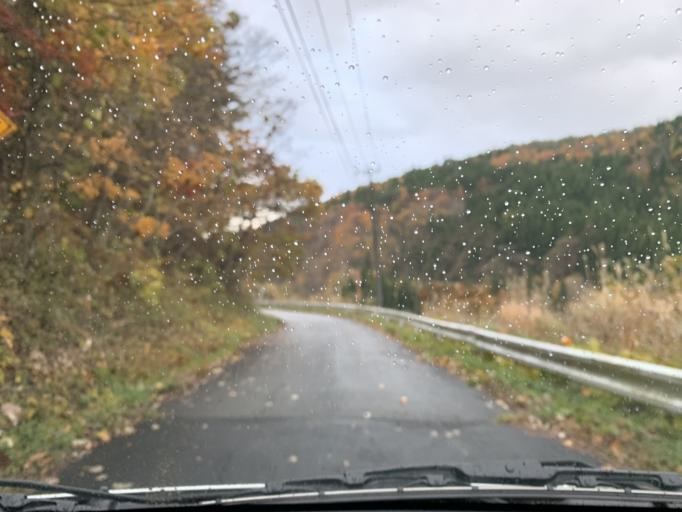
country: JP
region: Iwate
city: Mizusawa
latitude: 39.1009
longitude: 140.9671
